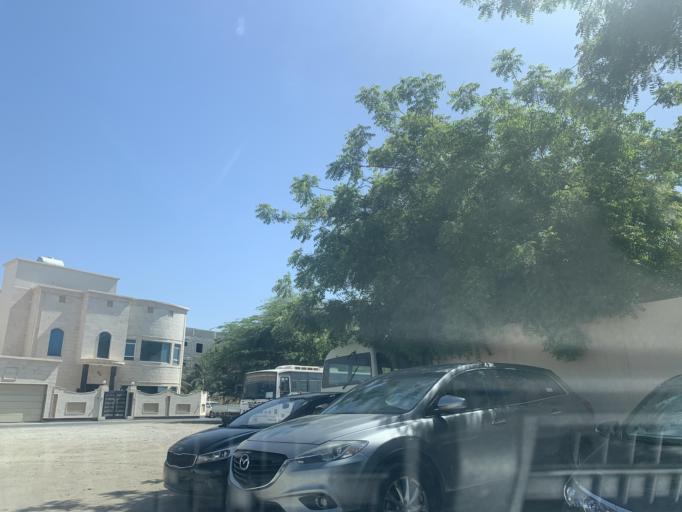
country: BH
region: Manama
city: Jidd Hafs
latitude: 26.2125
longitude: 50.5578
